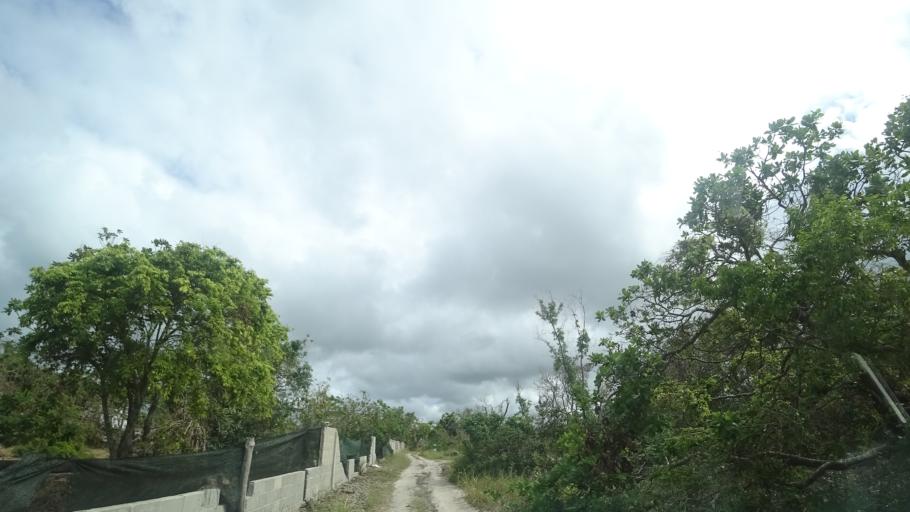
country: MZ
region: Sofala
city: Beira
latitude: -19.6119
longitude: 35.2216
